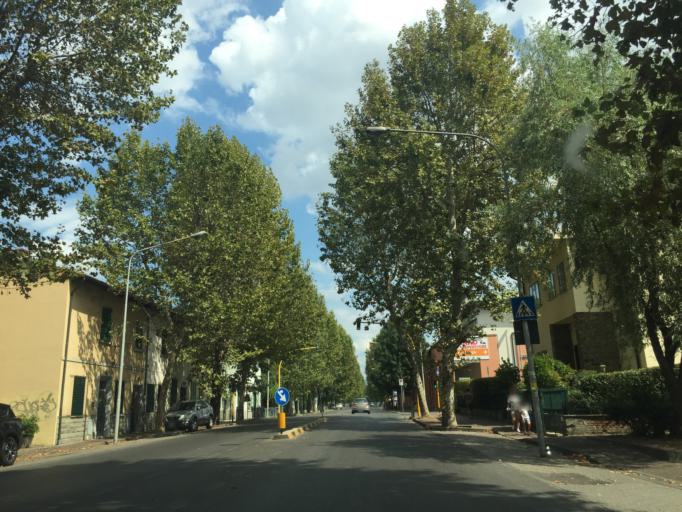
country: IT
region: Tuscany
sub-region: Province of Florence
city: Mantignano-Ugnano
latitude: 43.7939
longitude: 11.1849
